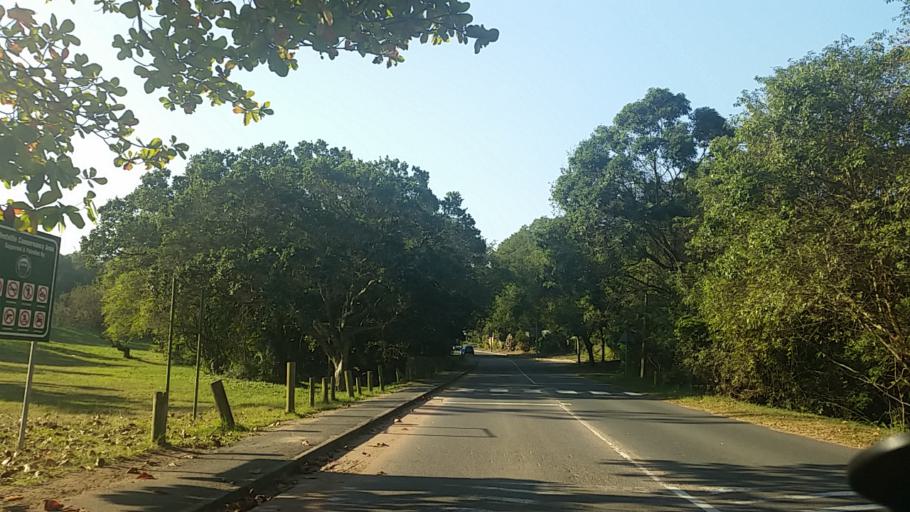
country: ZA
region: KwaZulu-Natal
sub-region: eThekwini Metropolitan Municipality
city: Berea
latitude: -29.8396
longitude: 30.9234
